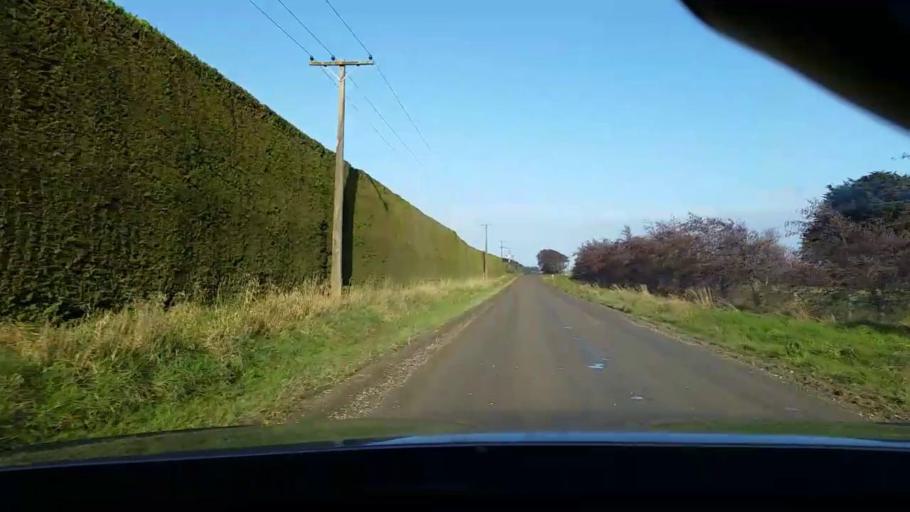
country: NZ
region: Southland
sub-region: Invercargill City
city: Invercargill
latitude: -46.3007
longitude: 168.3033
